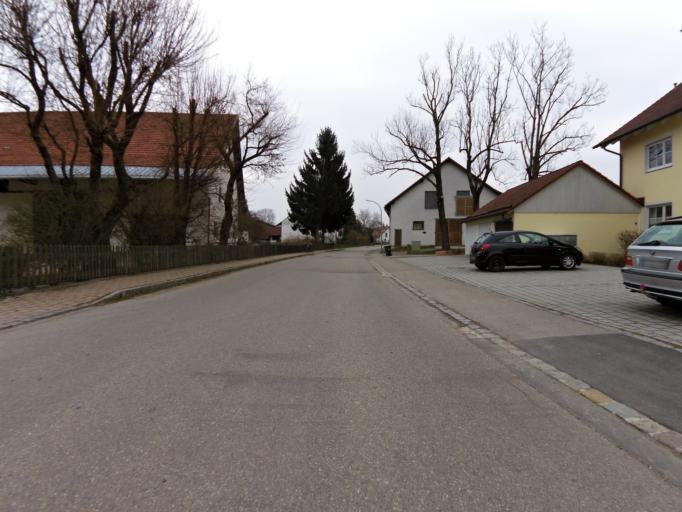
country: DE
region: Bavaria
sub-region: Upper Bavaria
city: Langenpreising
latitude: 48.4281
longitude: 11.9710
